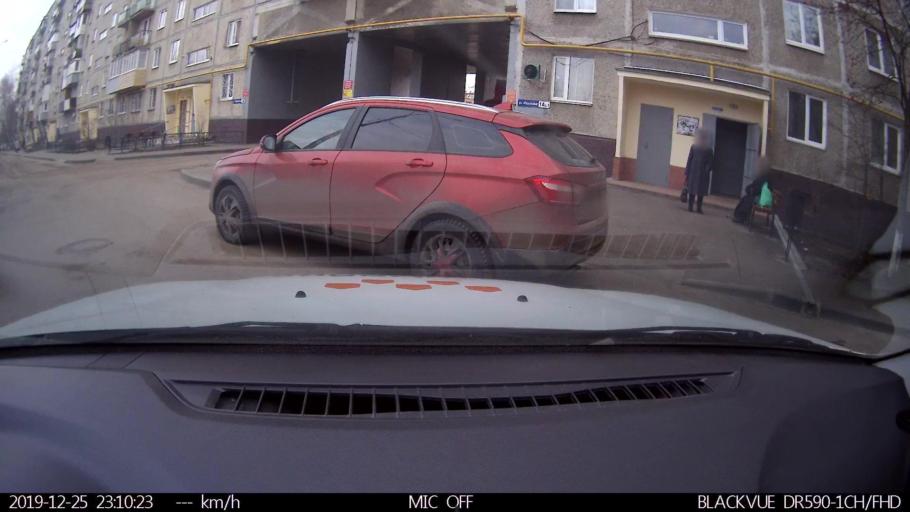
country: RU
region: Nizjnij Novgorod
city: Gorbatovka
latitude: 56.3607
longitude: 43.8230
